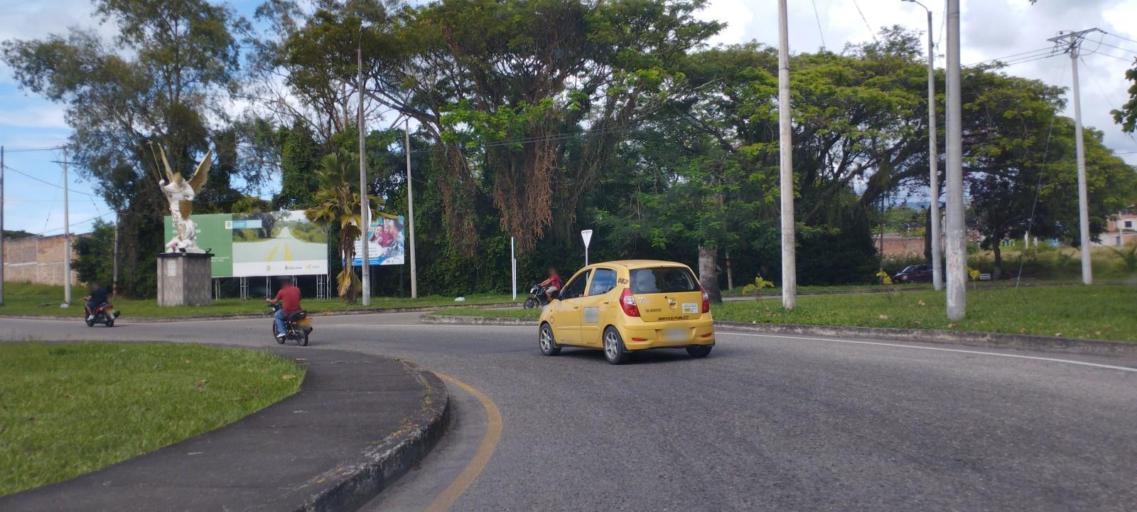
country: CO
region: Huila
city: Garzon
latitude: 2.1935
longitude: -75.6412
